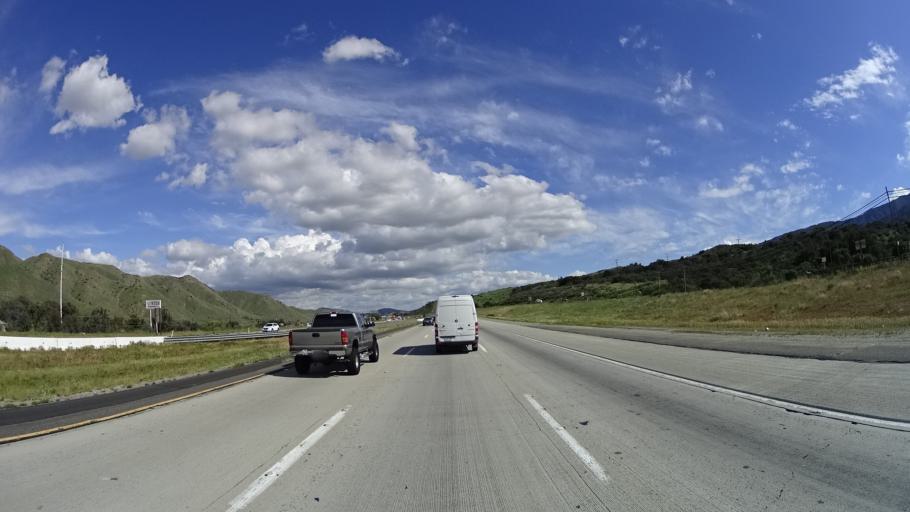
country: US
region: California
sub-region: Riverside County
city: El Cerrito
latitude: 33.7446
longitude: -117.4444
